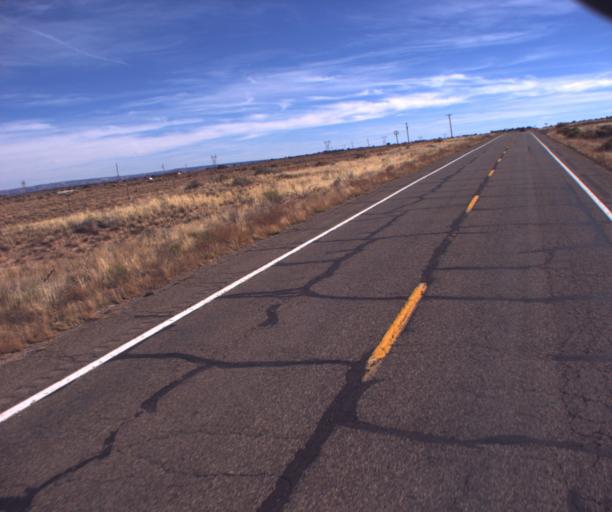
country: US
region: Arizona
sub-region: Coconino County
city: Kaibito
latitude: 36.6164
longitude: -110.9482
